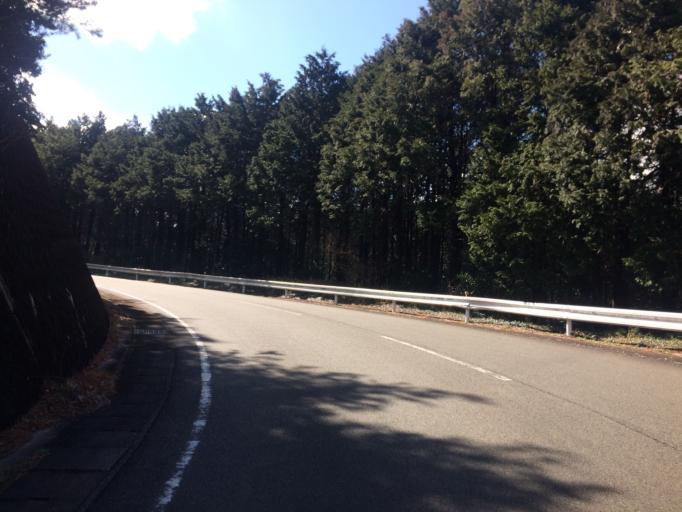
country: JP
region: Shizuoka
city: Shimada
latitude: 34.7599
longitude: 138.1760
